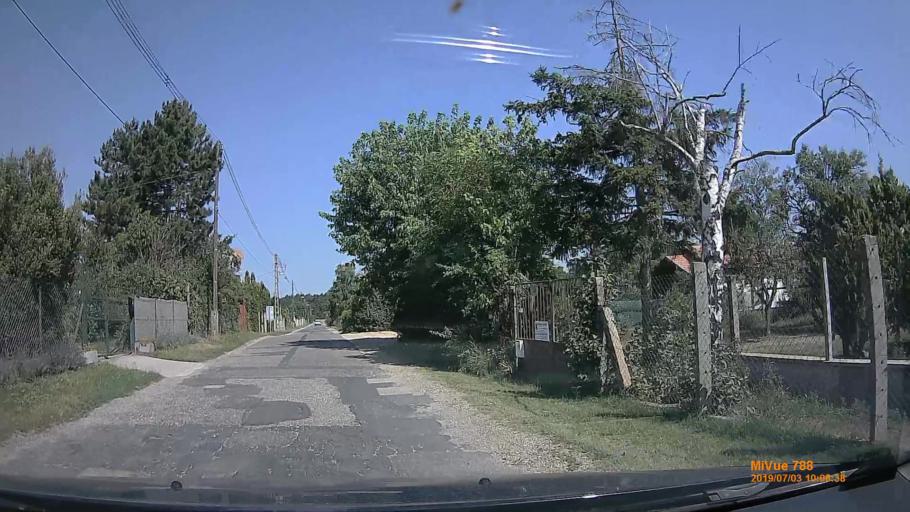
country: HU
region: Gyor-Moson-Sopron
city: Gyor
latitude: 47.7217
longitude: 17.7110
